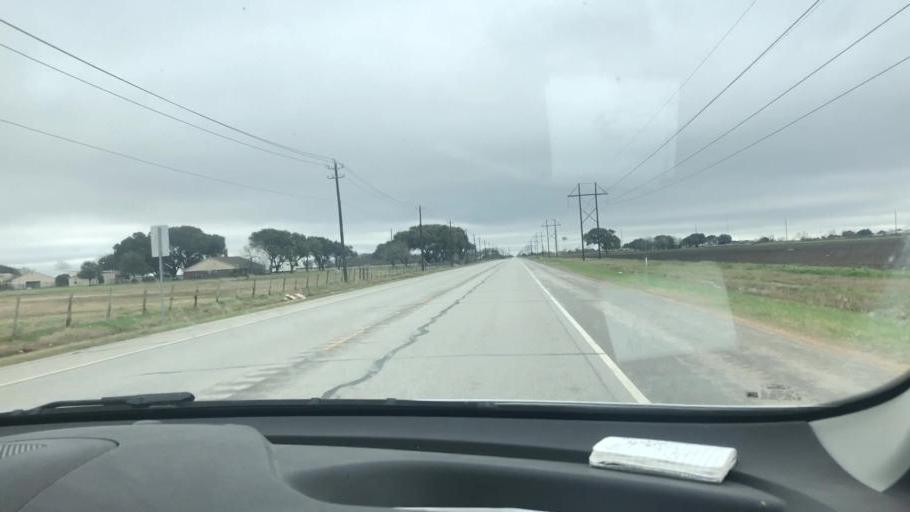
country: US
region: Texas
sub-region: Wharton County
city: Boling
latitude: 29.2048
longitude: -96.0229
